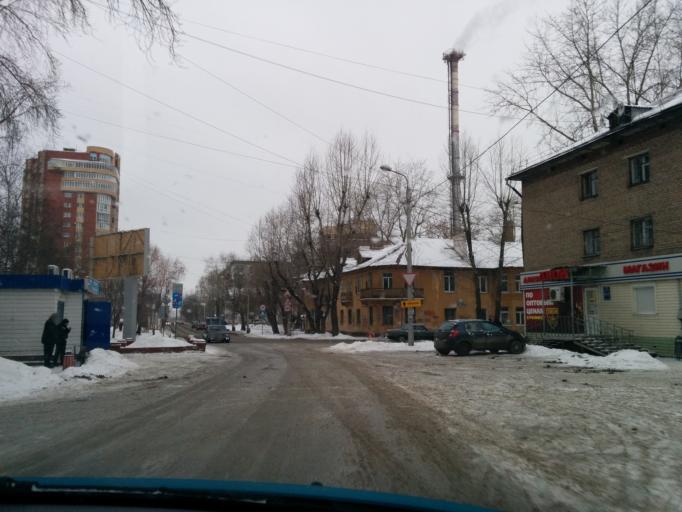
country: RU
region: Perm
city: Perm
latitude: 57.9992
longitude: 56.1777
